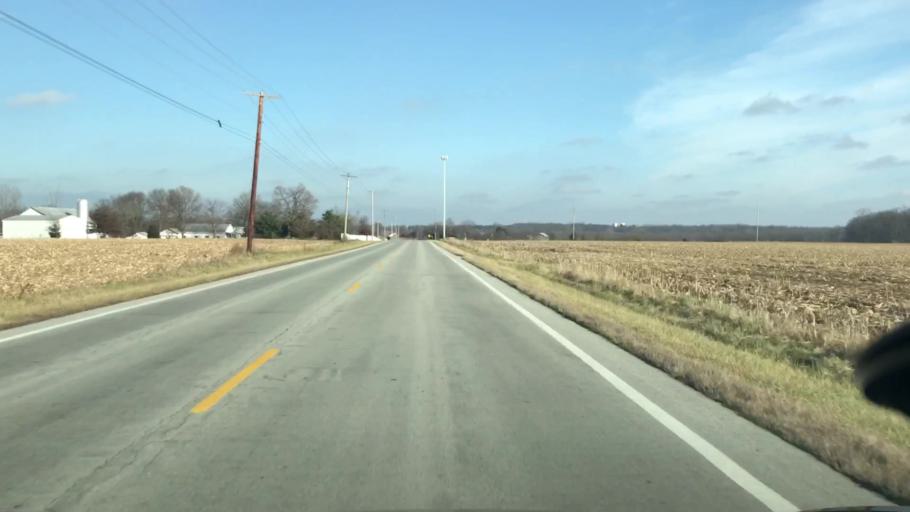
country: US
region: Ohio
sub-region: Greene County
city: Yellow Springs
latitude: 39.7944
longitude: -83.9401
